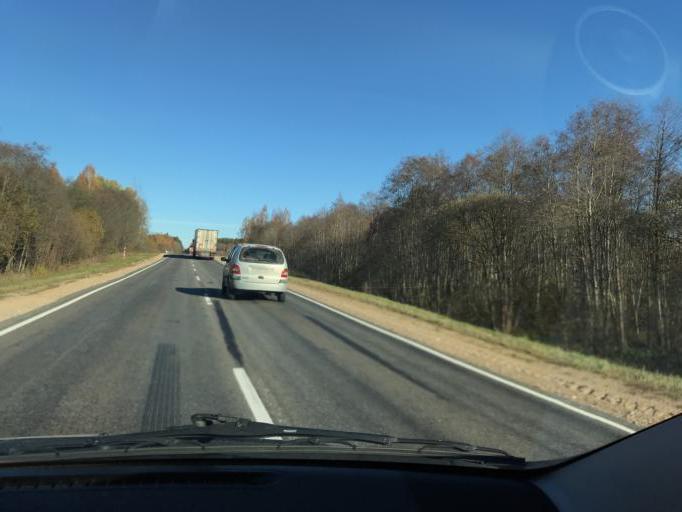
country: BY
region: Vitebsk
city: Polatsk
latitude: 55.3317
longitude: 28.7874
